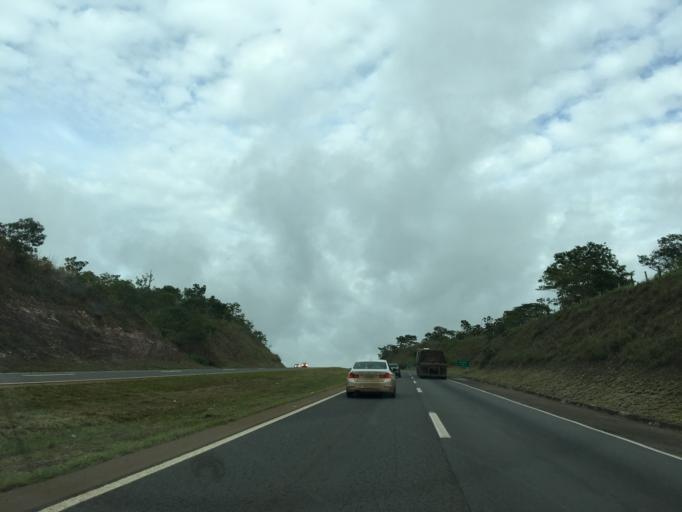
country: BR
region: Goias
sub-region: Abadiania
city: Abadiania
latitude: -16.1153
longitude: -48.3241
